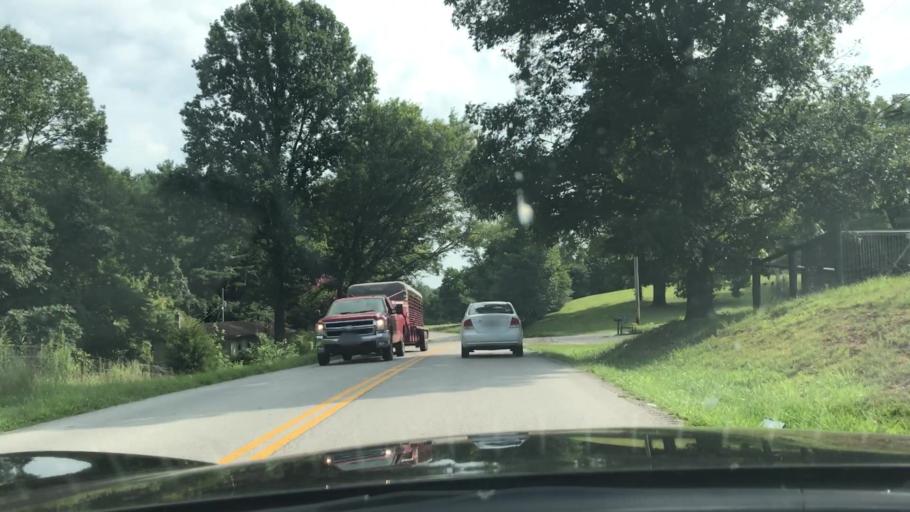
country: US
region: Kentucky
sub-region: Green County
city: Greensburg
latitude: 37.2767
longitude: -85.5233
